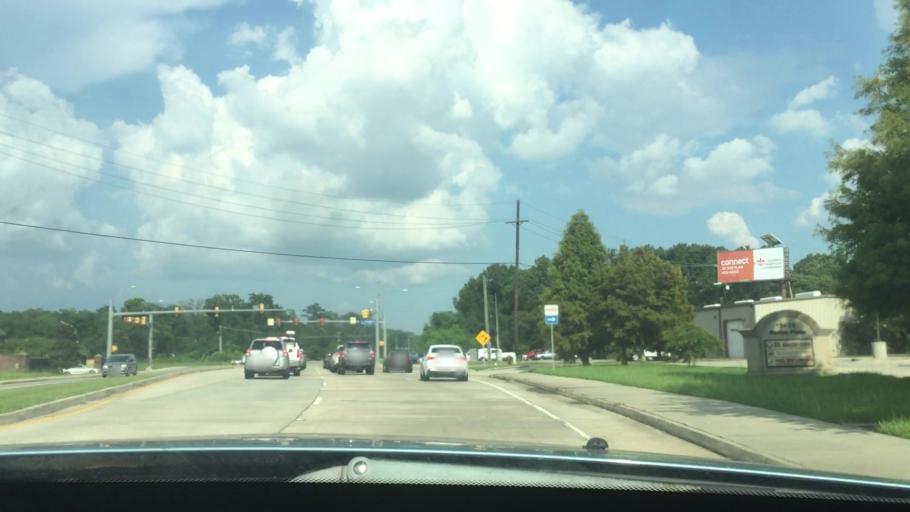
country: US
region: Louisiana
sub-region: East Baton Rouge Parish
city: Shenandoah
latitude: 30.4271
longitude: -91.0155
